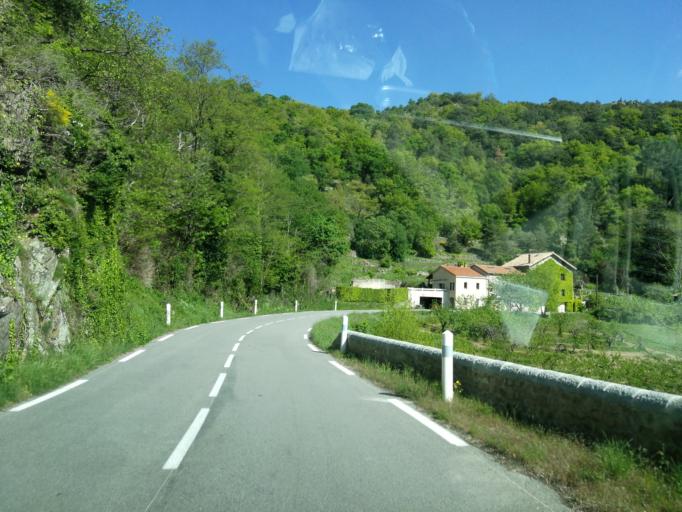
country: FR
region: Rhone-Alpes
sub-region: Departement de l'Ardeche
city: Saint-Sauveur-de-Montagut
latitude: 44.8589
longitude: 4.5596
